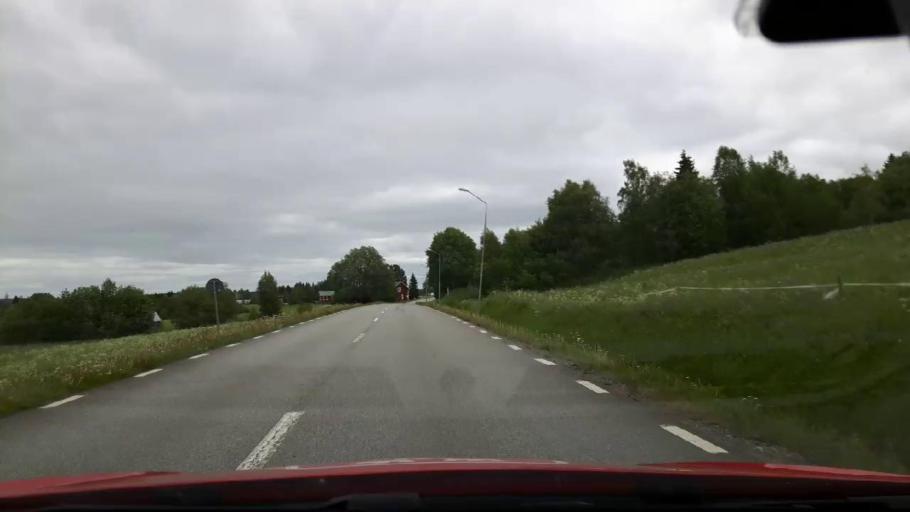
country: SE
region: Jaemtland
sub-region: Stroemsunds Kommun
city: Stroemsund
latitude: 63.5714
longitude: 15.3845
